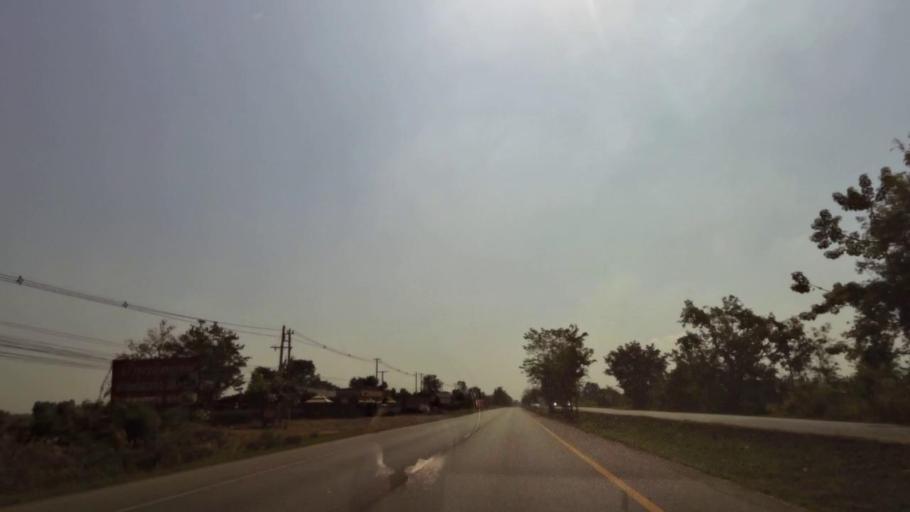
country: TH
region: Phichit
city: Bueng Na Rang
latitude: 16.3053
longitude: 100.1285
